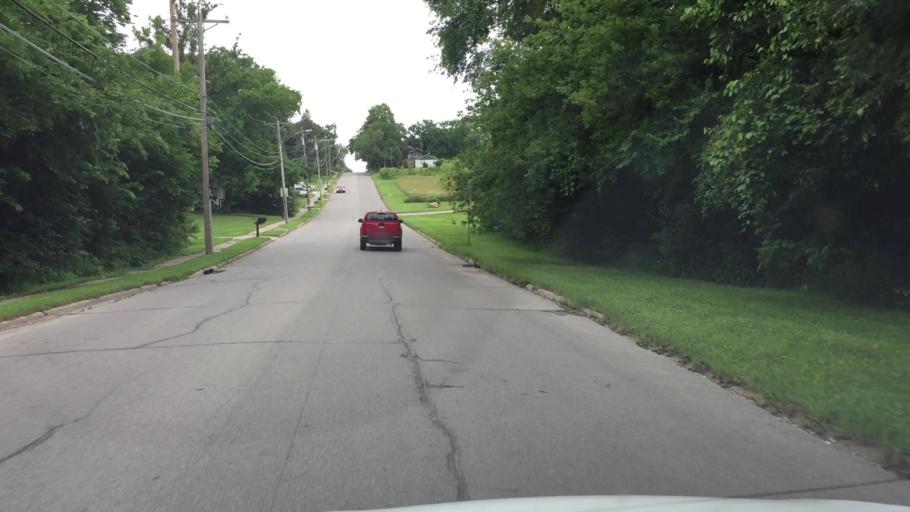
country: US
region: Iowa
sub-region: Jasper County
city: Newton
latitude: 41.7101
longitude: -93.0532
